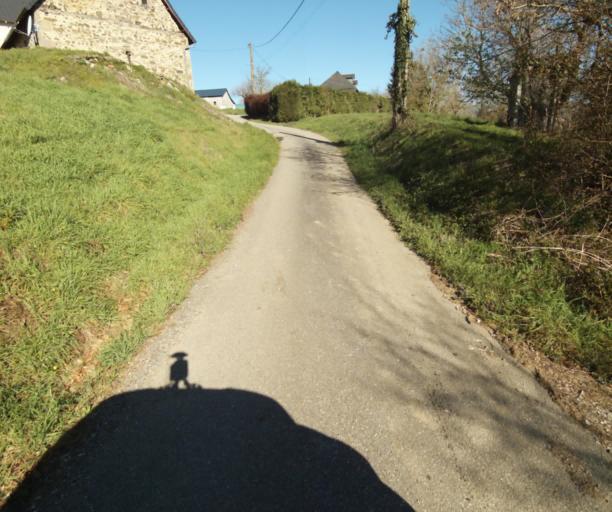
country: FR
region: Limousin
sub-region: Departement de la Correze
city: Chamboulive
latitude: 45.4042
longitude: 1.7150
